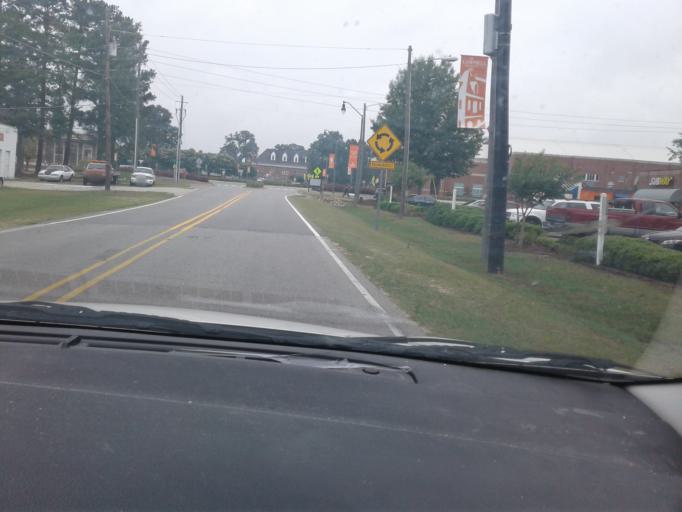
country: US
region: North Carolina
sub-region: Harnett County
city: Buies Creek
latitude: 35.4059
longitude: -78.7368
